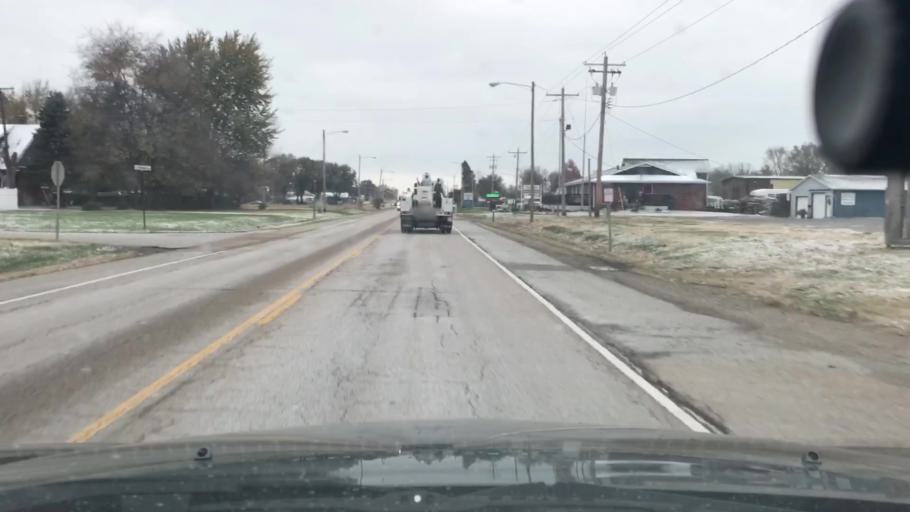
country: US
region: Illinois
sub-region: Madison County
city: Pontoon Beach
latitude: 38.7272
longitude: -90.0708
